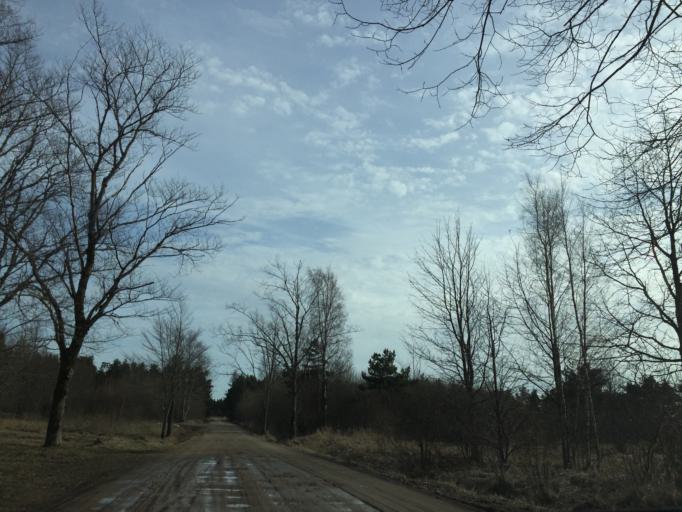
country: EE
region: Paernumaa
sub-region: Paernu linn
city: Parnu
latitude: 58.2423
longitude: 24.4827
